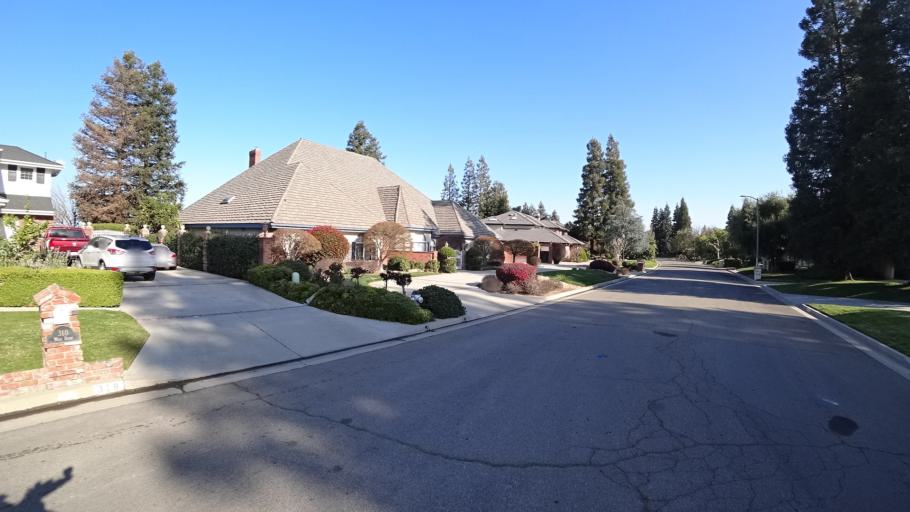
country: US
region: California
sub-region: Fresno County
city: Clovis
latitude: 36.8629
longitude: -119.7969
